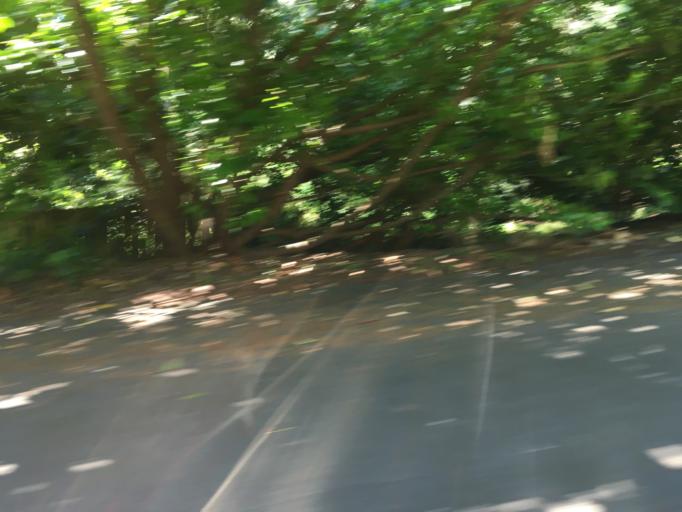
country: US
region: Washington
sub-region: King County
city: Redmond
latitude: 47.6437
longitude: -122.1547
